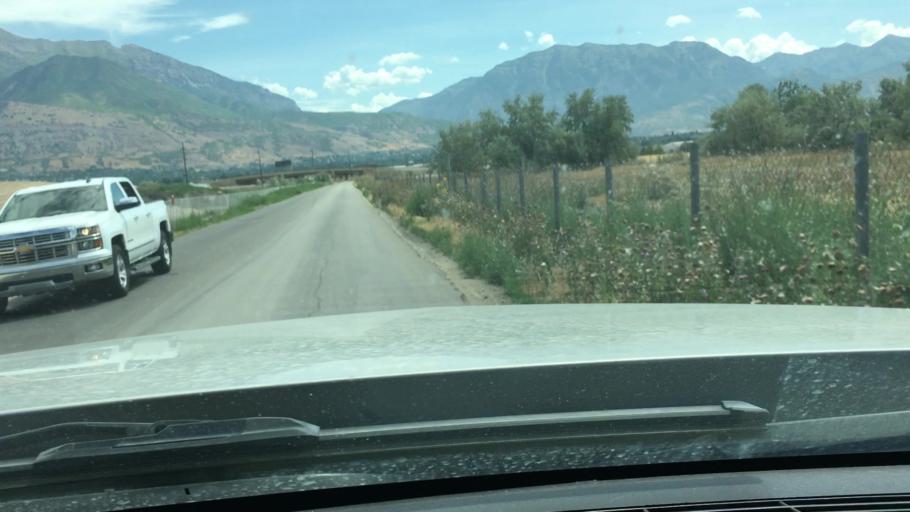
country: US
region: Utah
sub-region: Utah County
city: Pleasant Grove
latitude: 40.3434
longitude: -111.7625
